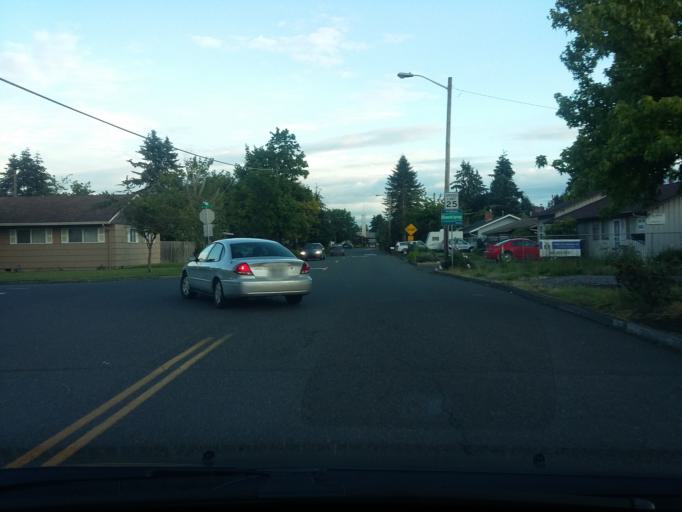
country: US
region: Washington
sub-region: Clark County
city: Orchards
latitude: 45.6204
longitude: -122.5645
